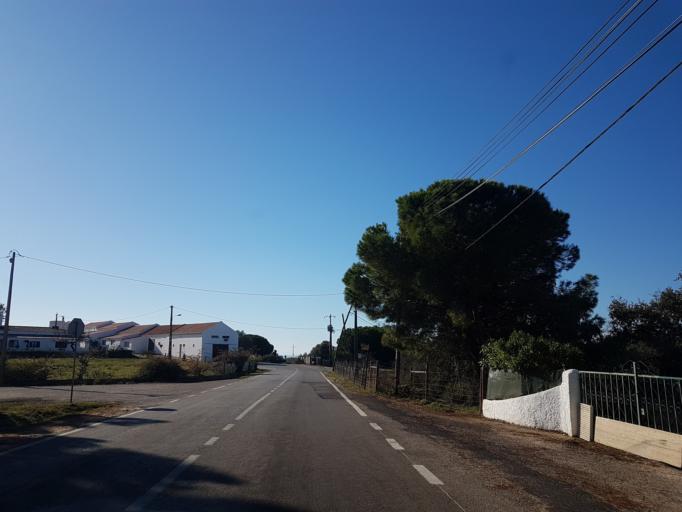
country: PT
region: Faro
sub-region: Lagoa
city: Carvoeiro
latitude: 37.1024
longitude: -8.4159
